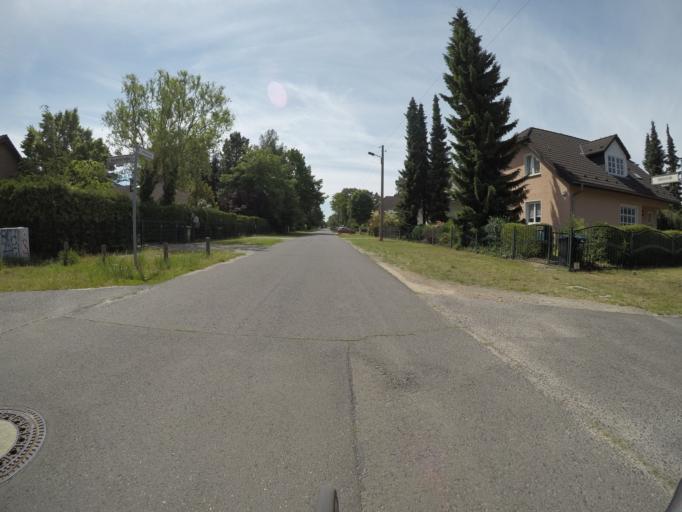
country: DE
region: Berlin
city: Mahlsdorf
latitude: 52.4799
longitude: 13.6119
